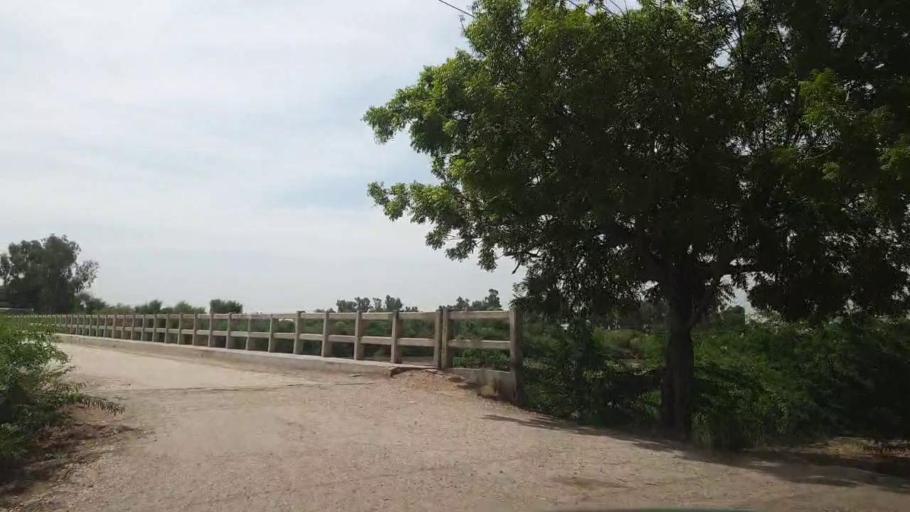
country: PK
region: Sindh
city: Kot Diji
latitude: 27.1262
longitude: 68.9988
